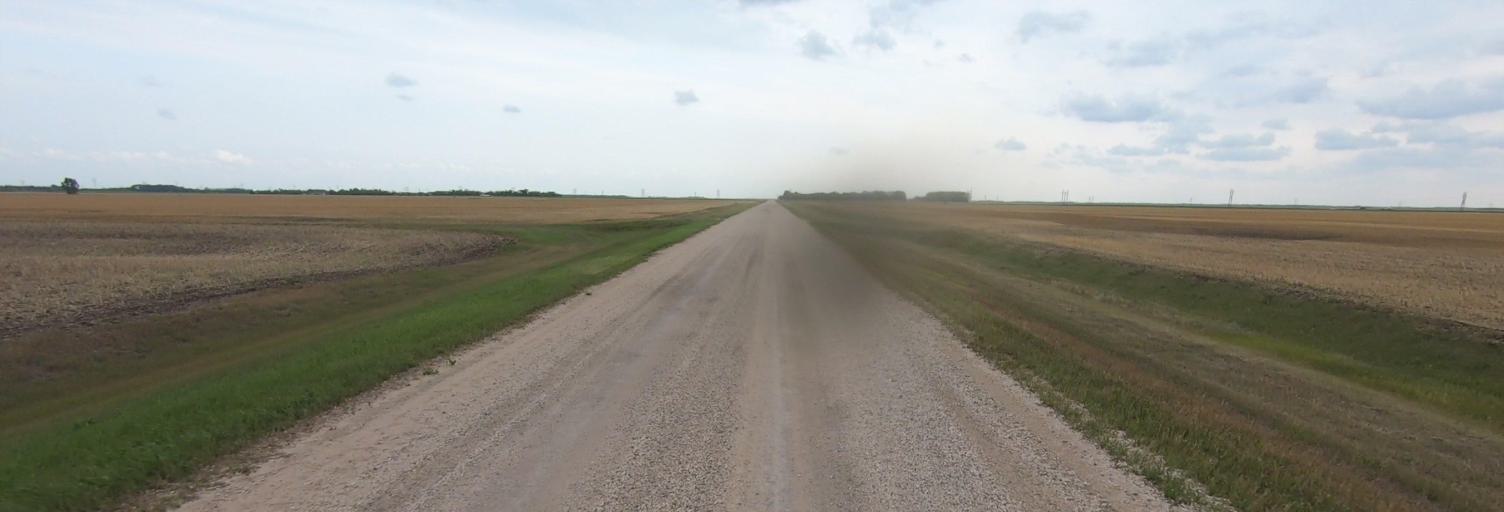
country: CA
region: Manitoba
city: Headingley
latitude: 49.7242
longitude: -97.3860
